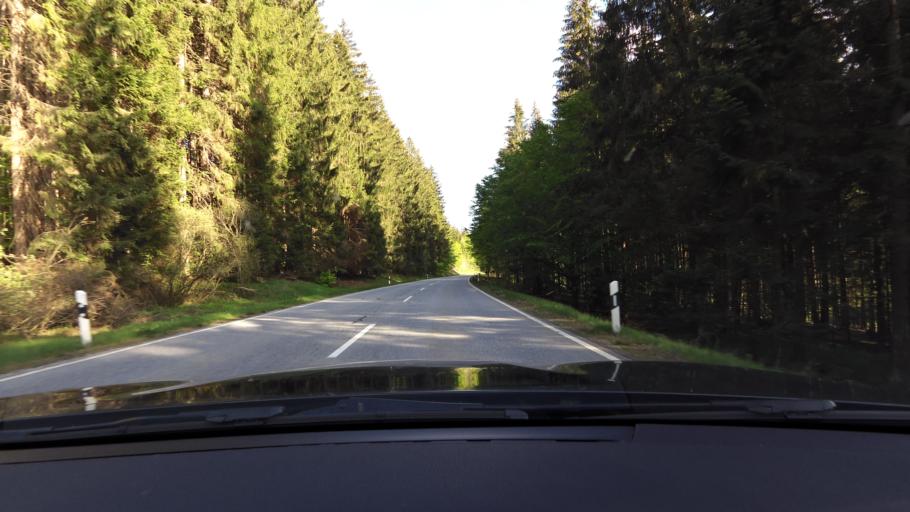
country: DE
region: Bavaria
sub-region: Lower Bavaria
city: Bayerisch Eisenstein
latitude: 49.0821
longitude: 13.2073
